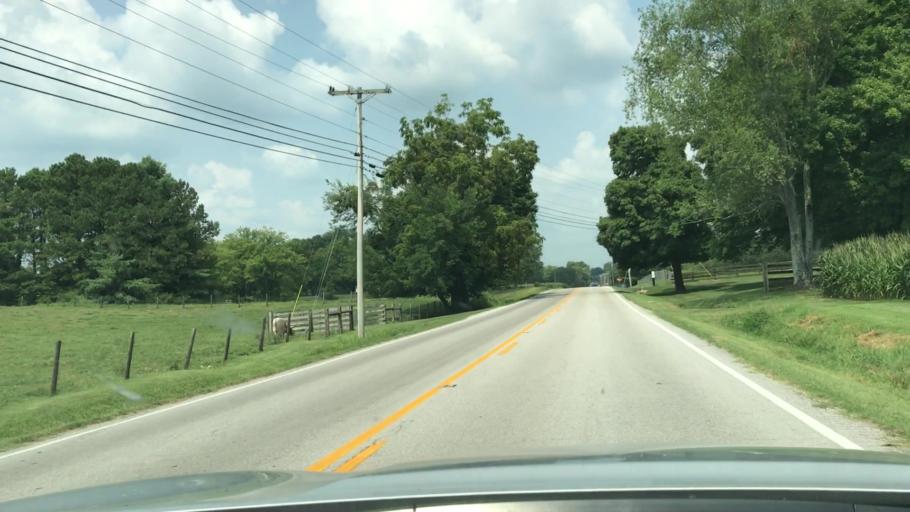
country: US
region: Kentucky
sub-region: Todd County
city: Elkton
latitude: 36.8063
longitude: -87.1335
